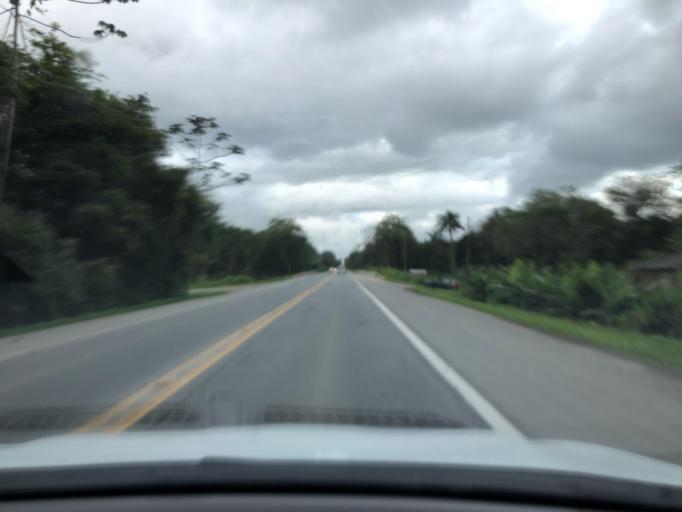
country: BR
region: Santa Catarina
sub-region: Sao Francisco Do Sul
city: Sao Francisco do Sul
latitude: -26.3284
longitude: -48.6507
